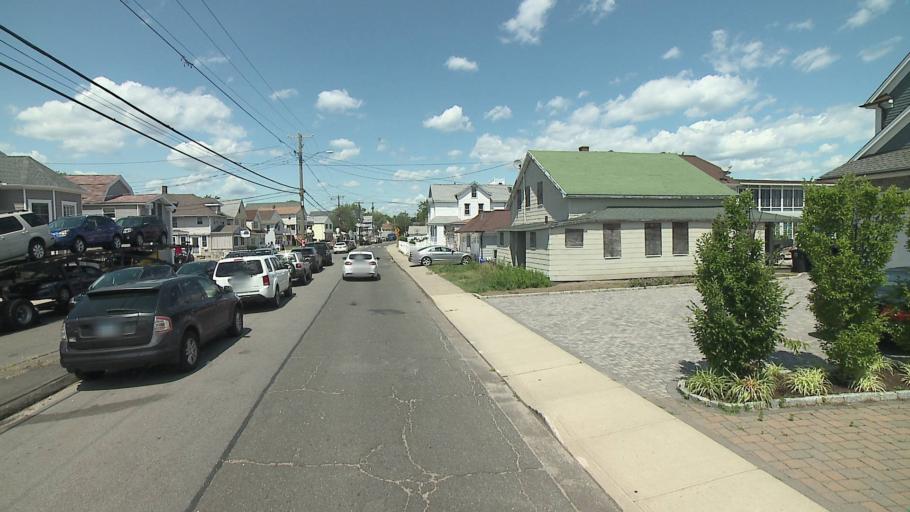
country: US
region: Connecticut
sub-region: New Haven County
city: Milford
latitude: 41.2048
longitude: -73.0625
